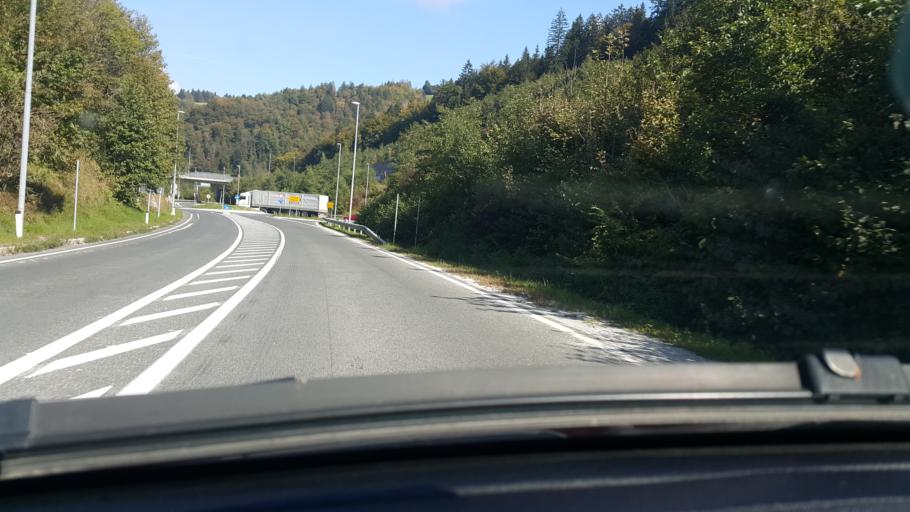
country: SI
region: Zagorje ob Savi
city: Izlake
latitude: 46.1916
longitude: 14.8993
